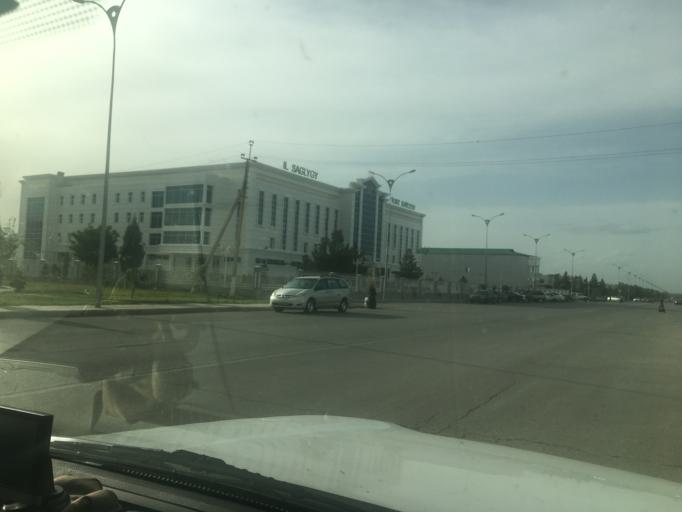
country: TM
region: Mary
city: Mary
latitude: 37.5821
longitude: 61.8707
